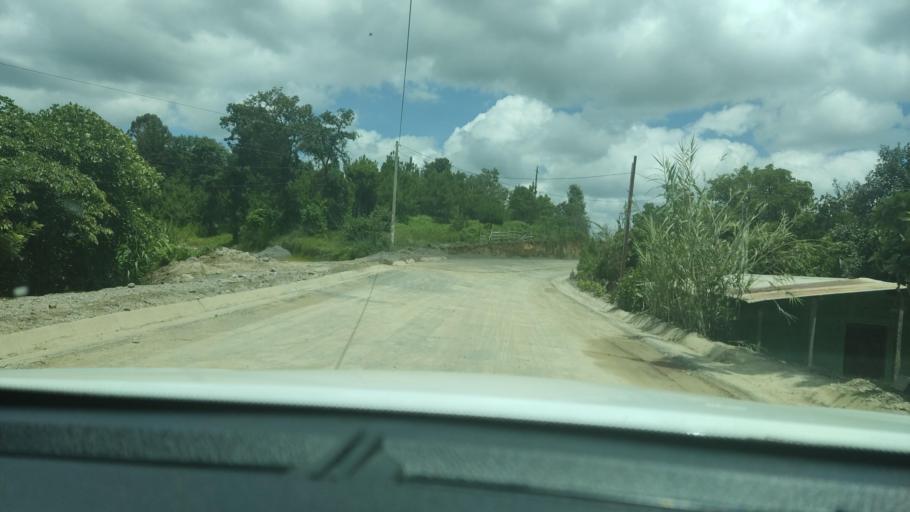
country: GT
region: Chimaltenango
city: San Martin Jilotepeque
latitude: 14.7915
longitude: -90.8046
